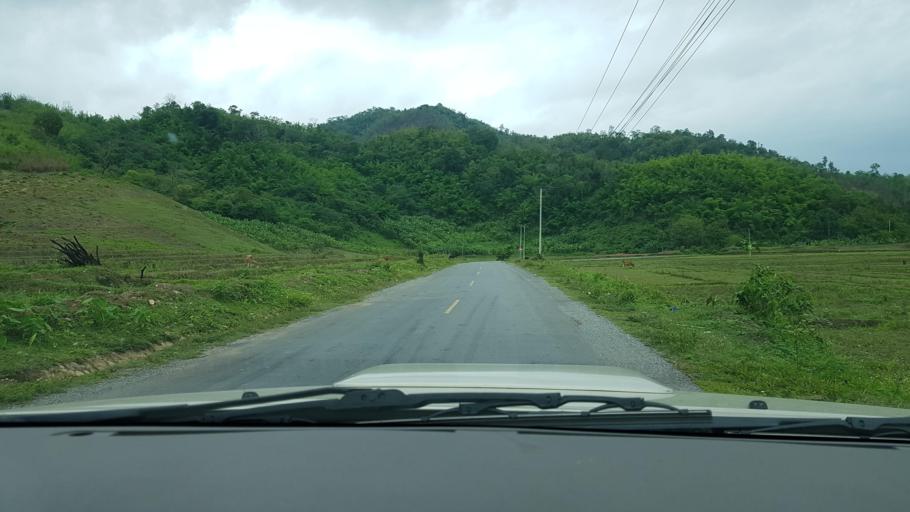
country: LA
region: Loungnamtha
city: Muang Nale
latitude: 20.3766
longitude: 101.7373
